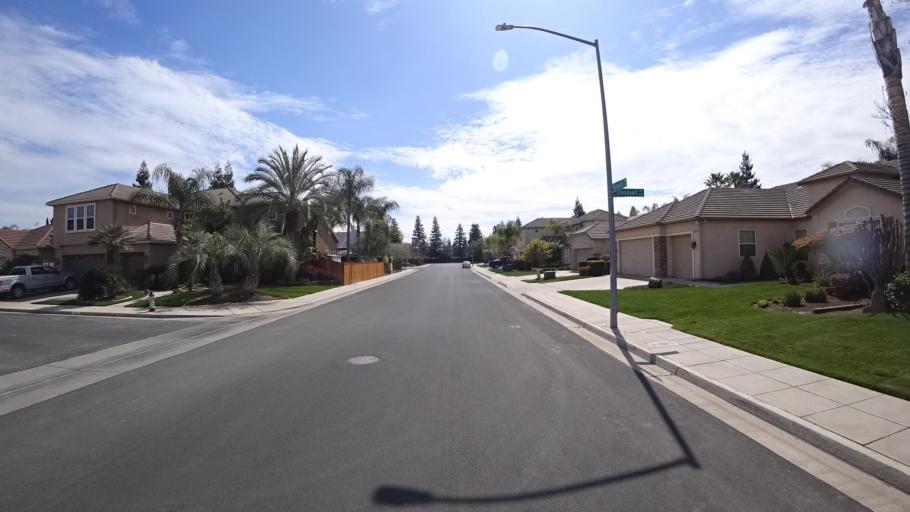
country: US
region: California
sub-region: Fresno County
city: Biola
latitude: 36.8419
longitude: -119.8969
